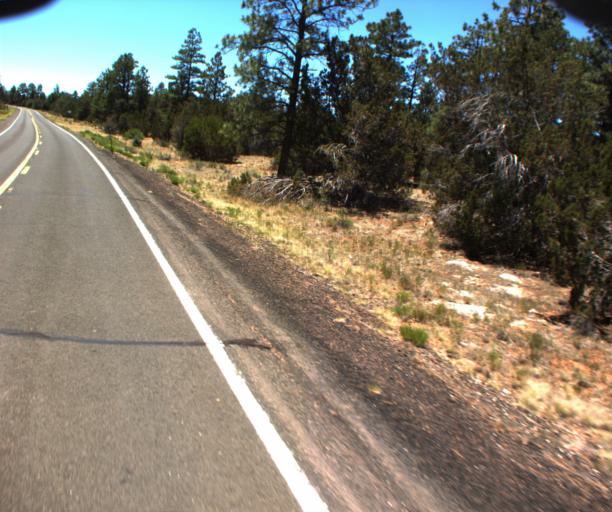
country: US
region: Arizona
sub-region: Gila County
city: Star Valley
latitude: 34.6891
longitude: -111.1114
